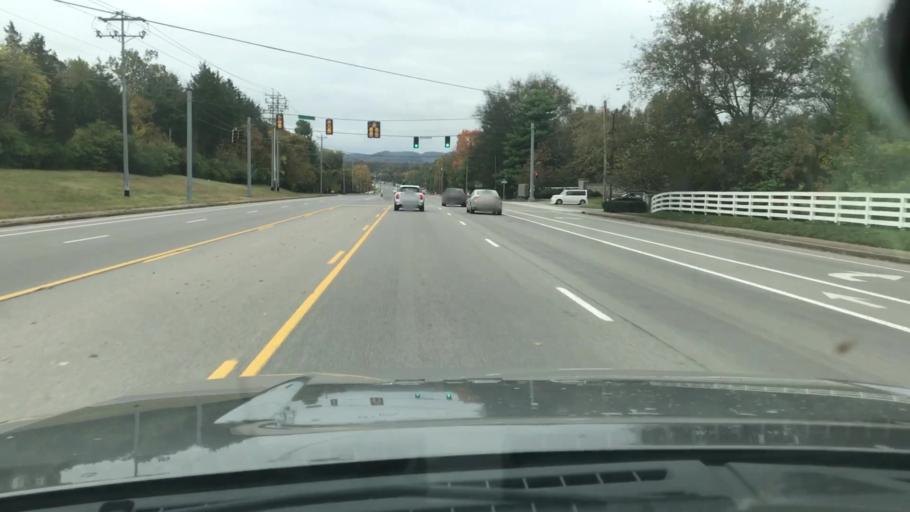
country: US
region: Tennessee
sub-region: Williamson County
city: Franklin
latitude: 35.9691
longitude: -86.8841
